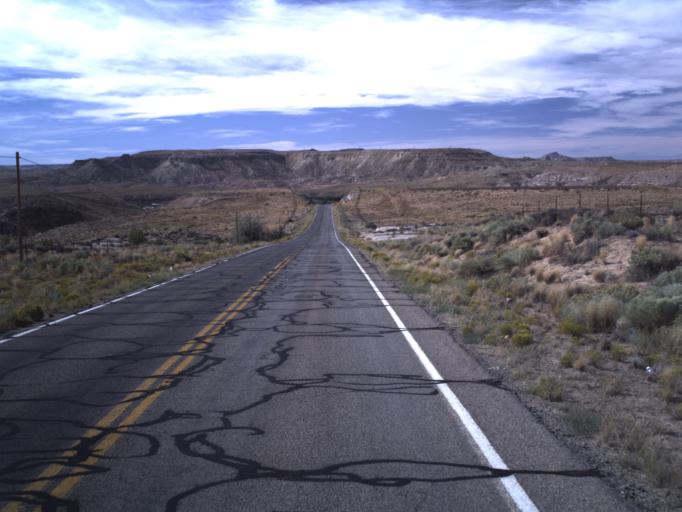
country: US
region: Utah
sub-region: San Juan County
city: Blanding
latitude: 37.2733
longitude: -109.2990
